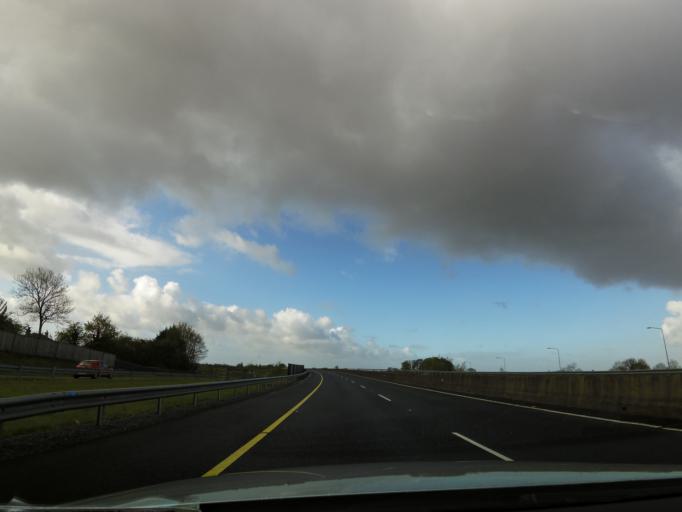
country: IE
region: Munster
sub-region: County Limerick
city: Annacotty
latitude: 52.6771
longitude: -8.5132
